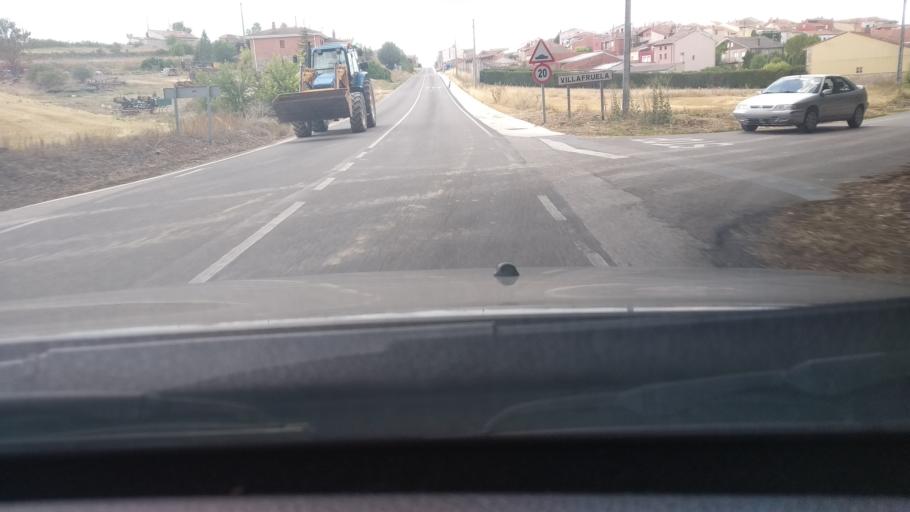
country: ES
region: Castille and Leon
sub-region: Provincia de Burgos
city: Villafruela
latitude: 41.9192
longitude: -3.9078
